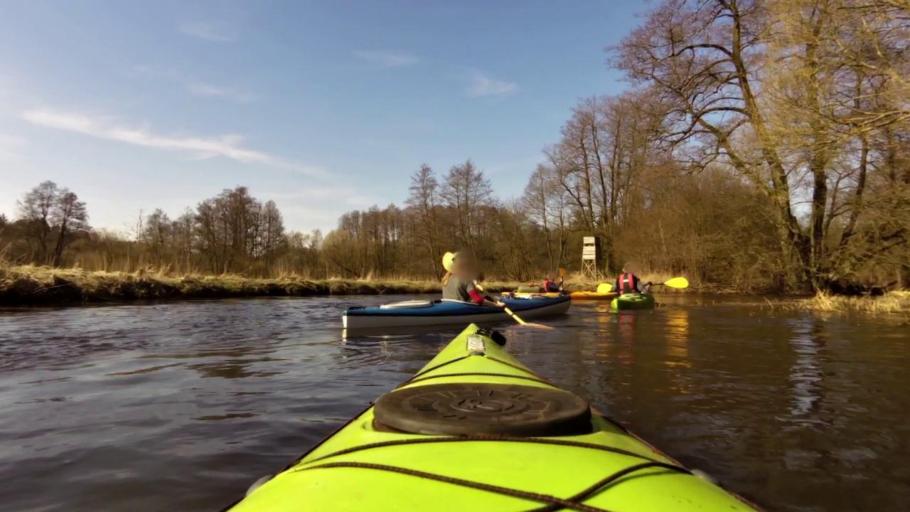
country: PL
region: West Pomeranian Voivodeship
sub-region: Powiat lobeski
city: Lobez
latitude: 53.7007
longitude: 15.5552
